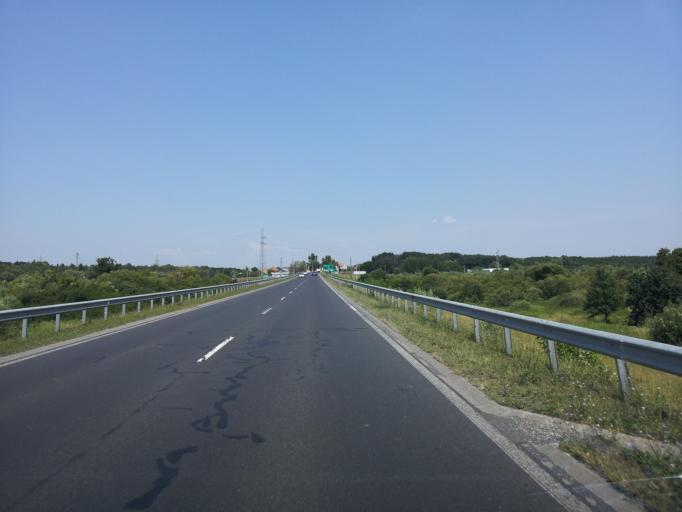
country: HU
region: Zala
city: Zalaegerszeg
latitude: 46.8573
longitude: 16.8576
